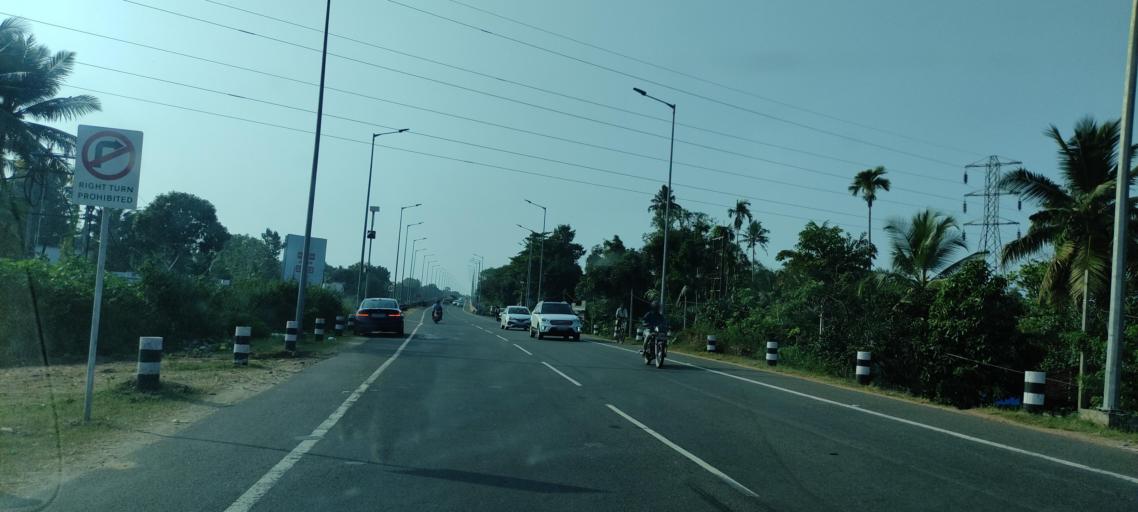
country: IN
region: Kerala
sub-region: Alappuzha
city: Alleppey
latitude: 9.4722
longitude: 76.3342
